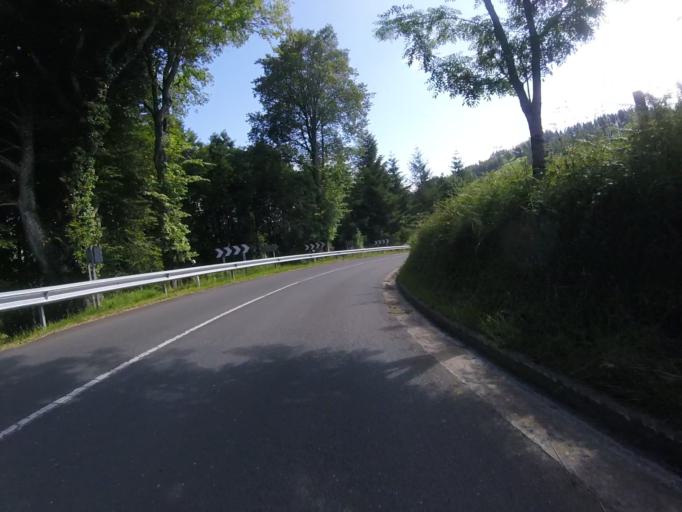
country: ES
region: Basque Country
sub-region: Provincia de Guipuzcoa
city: Ormaiztegui
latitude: 43.0882
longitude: -2.2455
